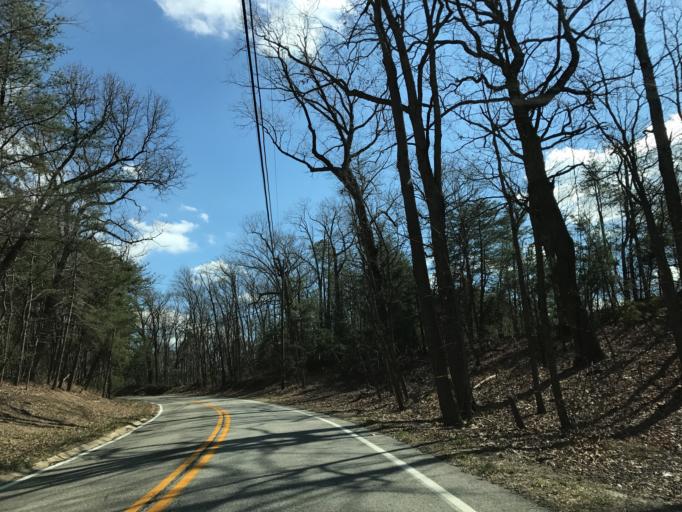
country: US
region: Maryland
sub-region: Anne Arundel County
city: Pasadena
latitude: 39.1314
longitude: -76.5807
